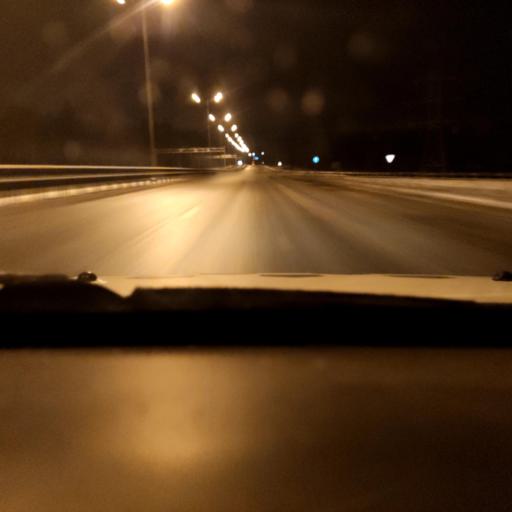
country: RU
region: Perm
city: Novyye Lyady
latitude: 58.0482
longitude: 56.4299
